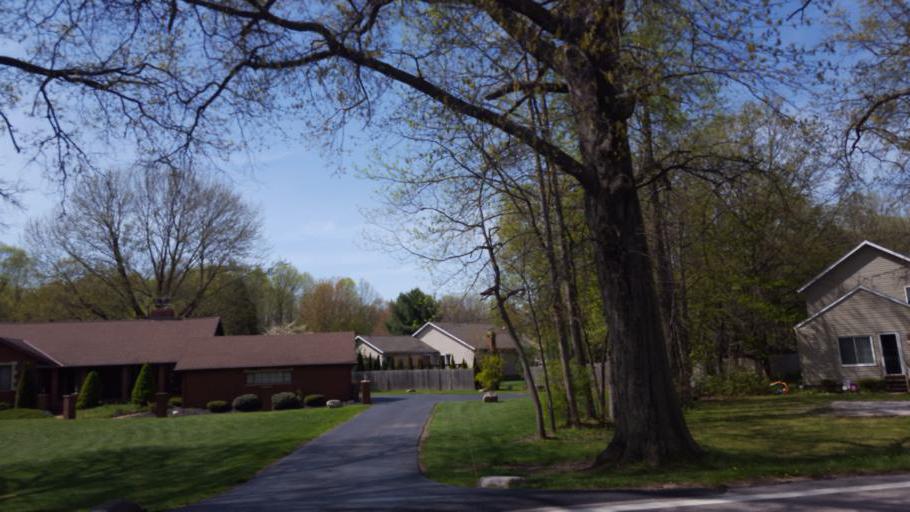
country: US
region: Ohio
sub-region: Lake County
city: Fairport Harbor
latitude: 41.7239
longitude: -81.3099
